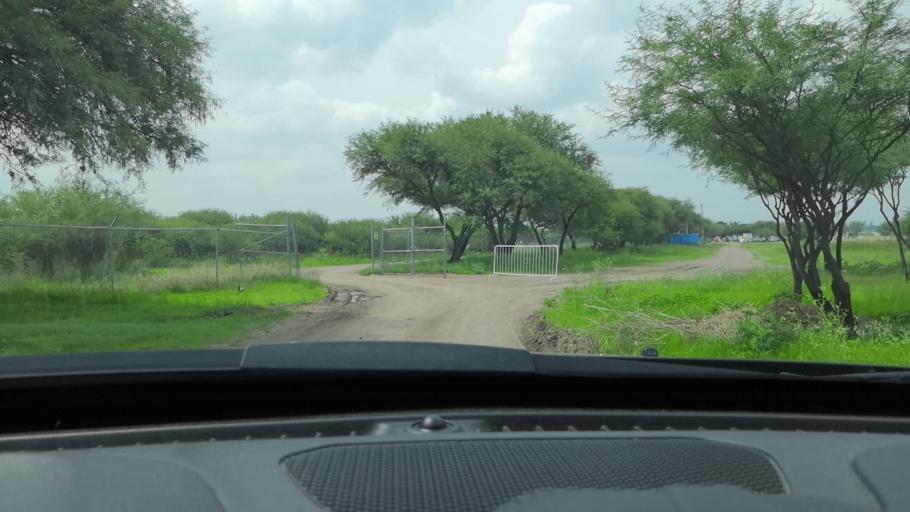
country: MX
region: Guanajuato
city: Leon
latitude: 21.1915
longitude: -101.6833
